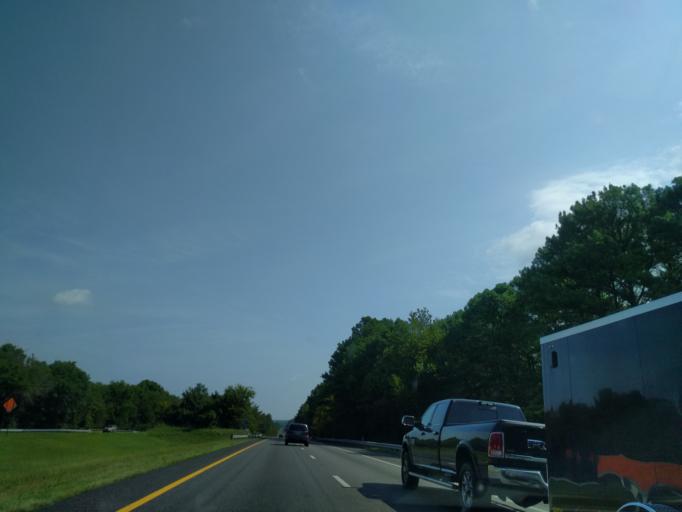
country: US
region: Tennessee
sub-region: Robertson County
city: Cross Plains
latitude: 36.5558
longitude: -86.6282
